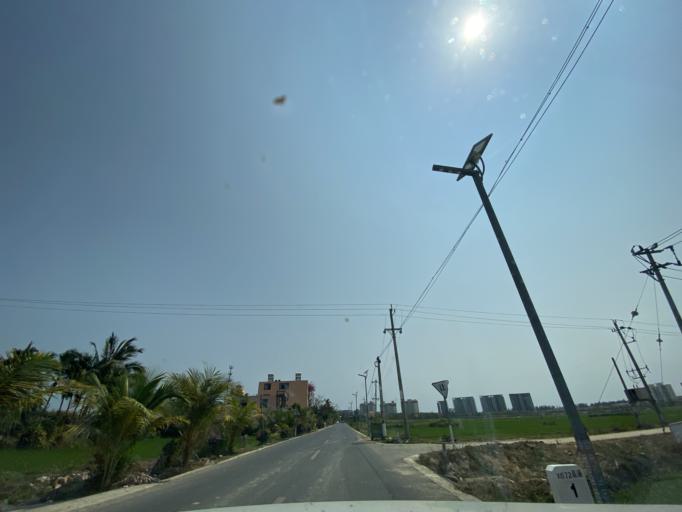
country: CN
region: Hainan
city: Yingzhou
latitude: 18.4116
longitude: 109.8152
